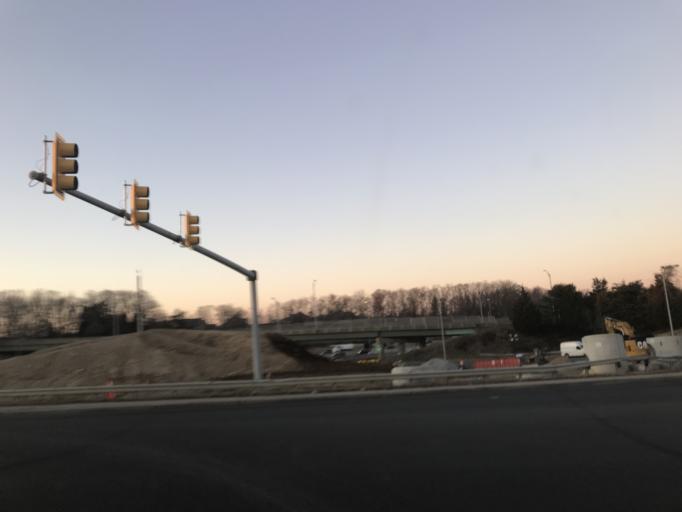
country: US
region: Virginia
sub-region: Fairfax County
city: Franconia
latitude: 38.8016
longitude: -77.1614
